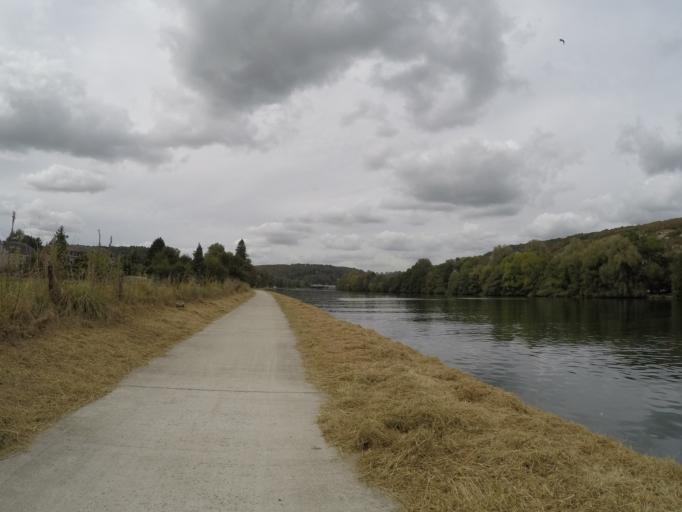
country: BE
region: Wallonia
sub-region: Province de Namur
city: Anhee
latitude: 50.3082
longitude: 4.8866
